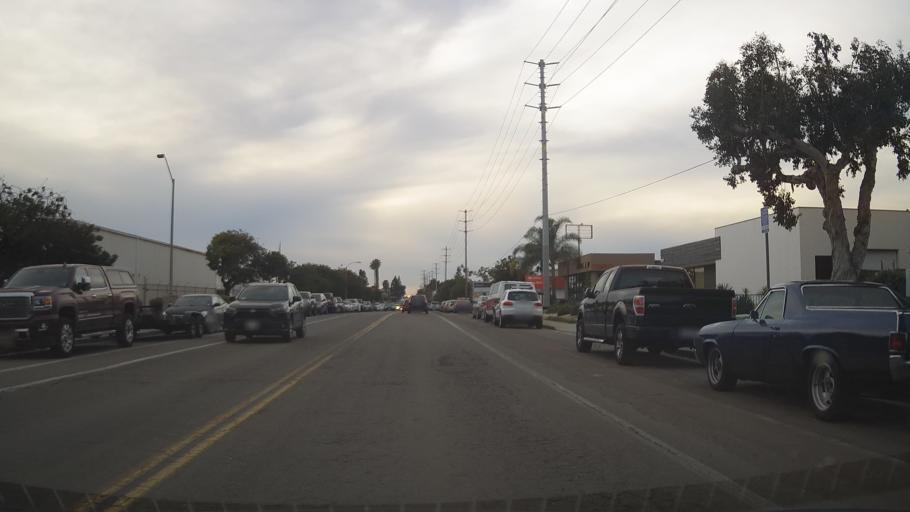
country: US
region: California
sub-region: San Diego County
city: San Diego
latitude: 32.8292
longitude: -117.1499
